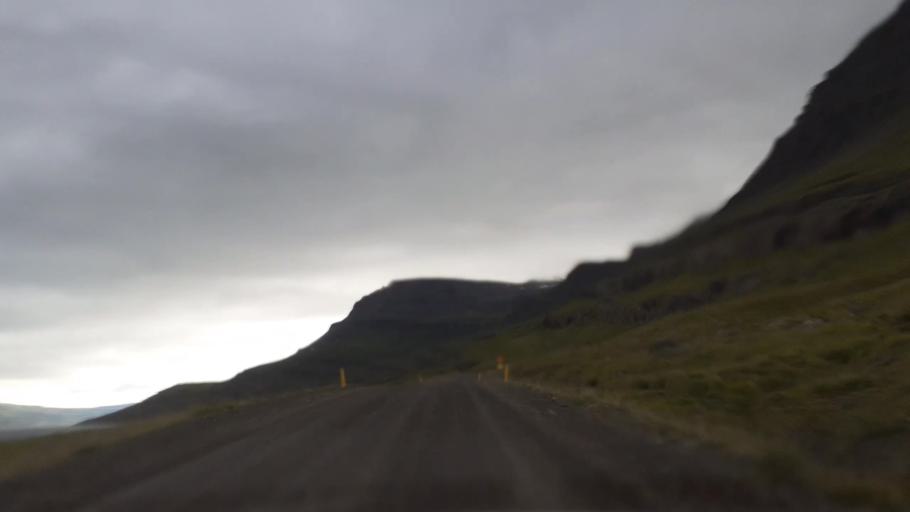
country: IS
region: East
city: Reydarfjoerdur
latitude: 65.0141
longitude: -14.1895
